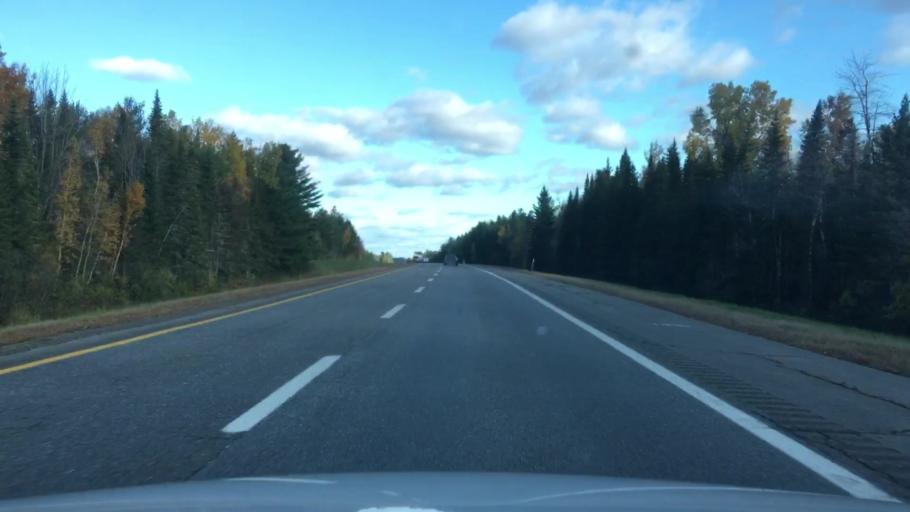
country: US
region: Maine
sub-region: Penobscot County
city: Greenbush
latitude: 45.1235
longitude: -68.6944
